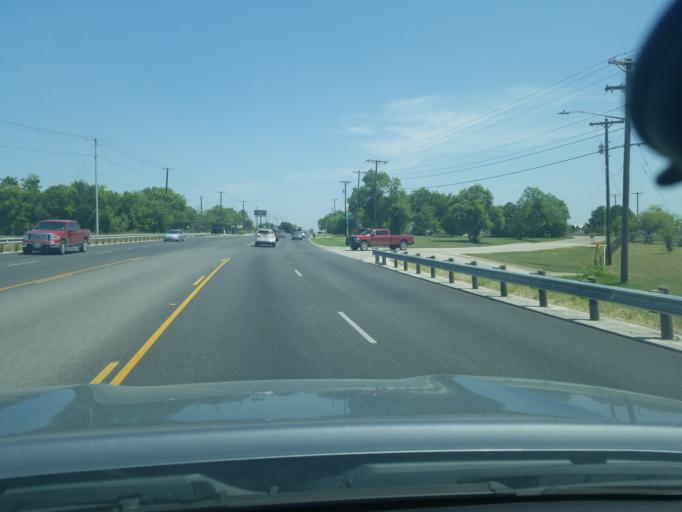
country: US
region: Texas
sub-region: Guadalupe County
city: Lake Dunlap
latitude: 29.6870
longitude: -98.0676
